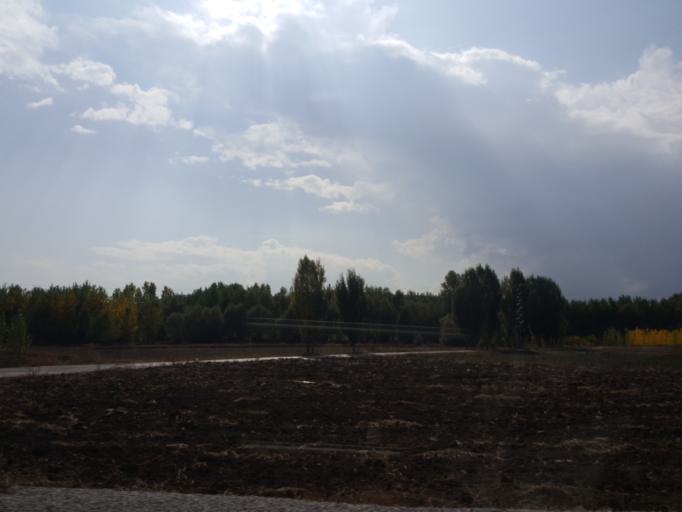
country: TR
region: Corum
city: Alaca
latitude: 40.1393
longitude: 34.8149
